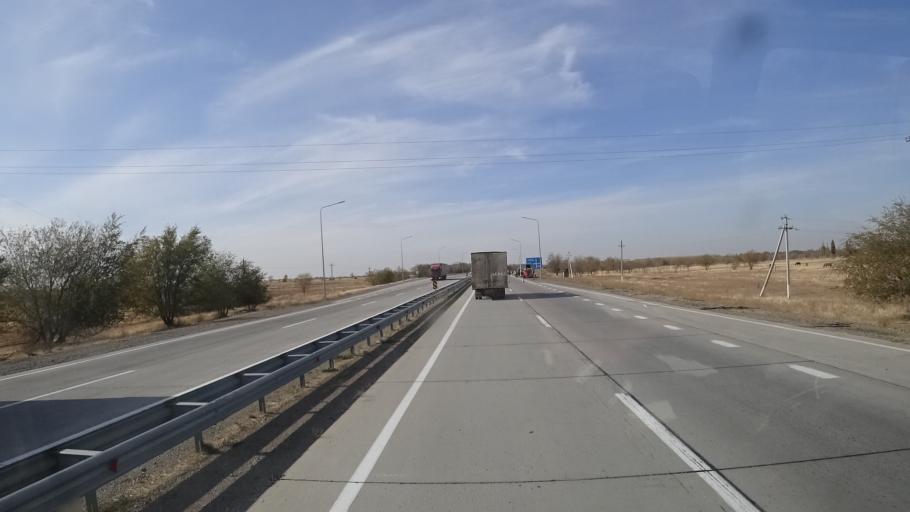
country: KZ
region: Zhambyl
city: Lugovoy
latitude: 42.9068
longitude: 72.9078
